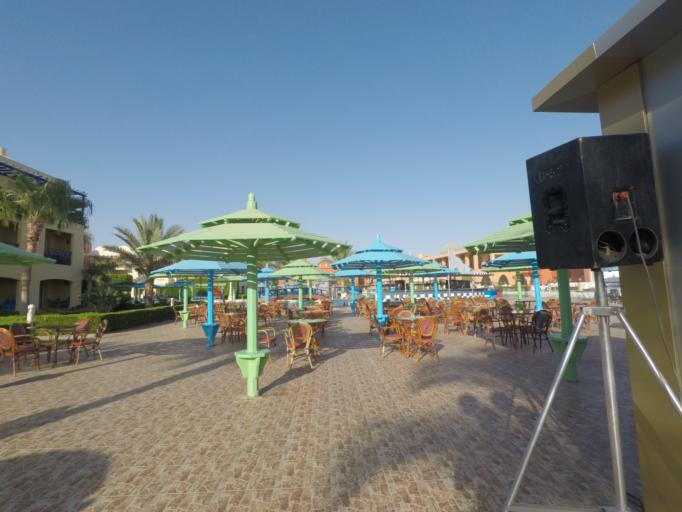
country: EG
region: Red Sea
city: Makadi Bay
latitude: 27.0900
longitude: 33.8499
